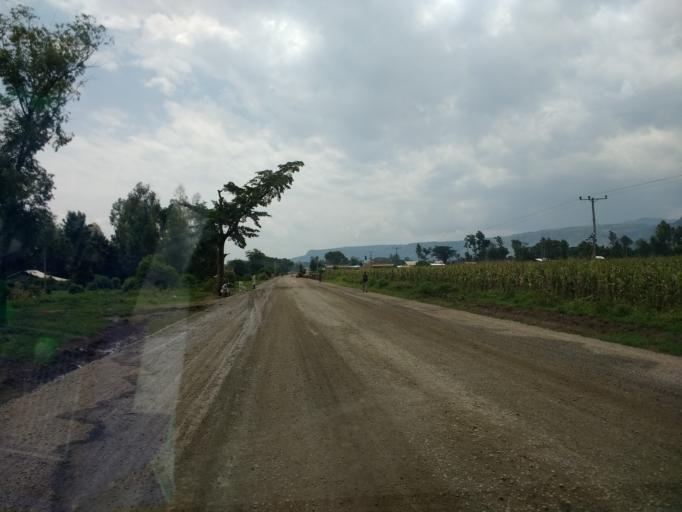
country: UG
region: Eastern Region
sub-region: Sironko District
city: Sironko
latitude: 1.2910
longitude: 34.2831
